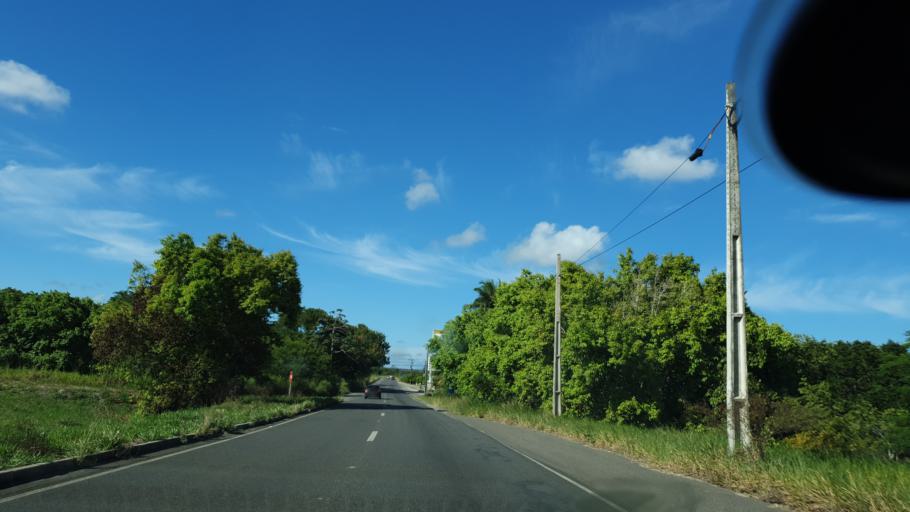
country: BR
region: Bahia
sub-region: Camacari
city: Camacari
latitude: -12.6753
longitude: -38.3007
